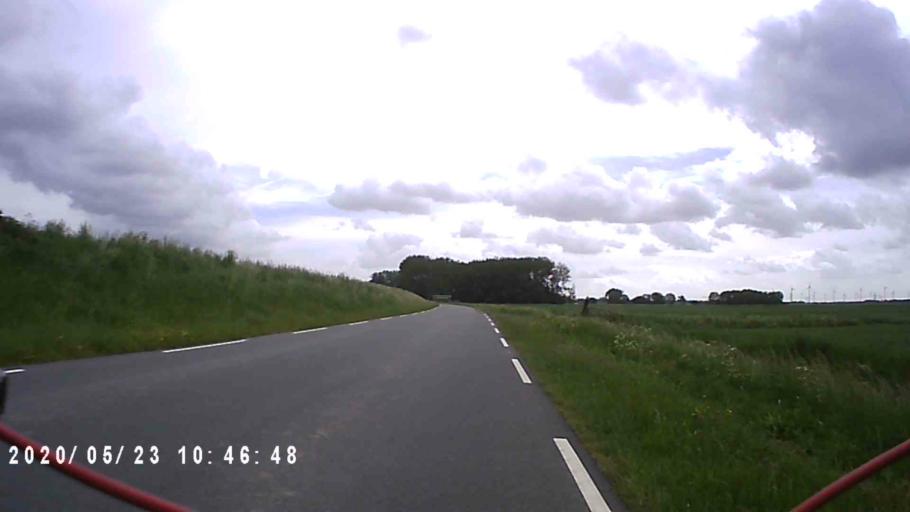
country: NL
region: Groningen
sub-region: Gemeente Delfzijl
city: Delfzijl
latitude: 53.3115
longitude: 6.9212
